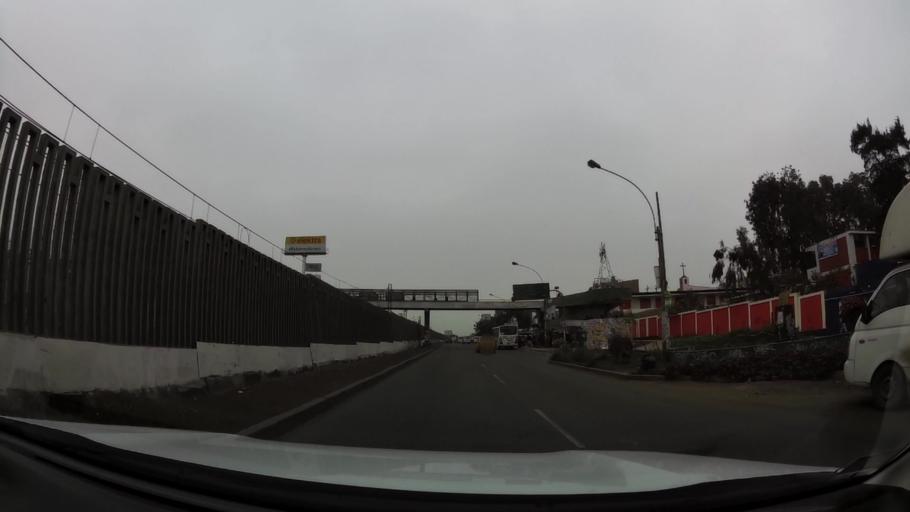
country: PE
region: Lima
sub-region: Lima
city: Surco
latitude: -12.1664
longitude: -76.9523
